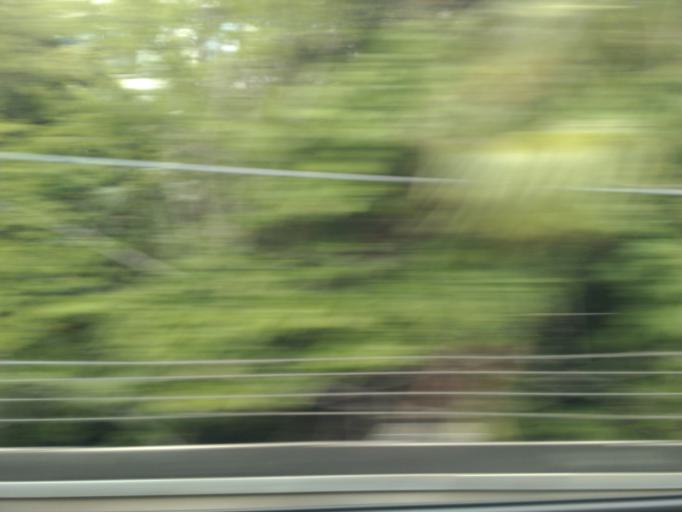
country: JP
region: Kanagawa
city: Yokohama
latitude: 35.4907
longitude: 139.5945
